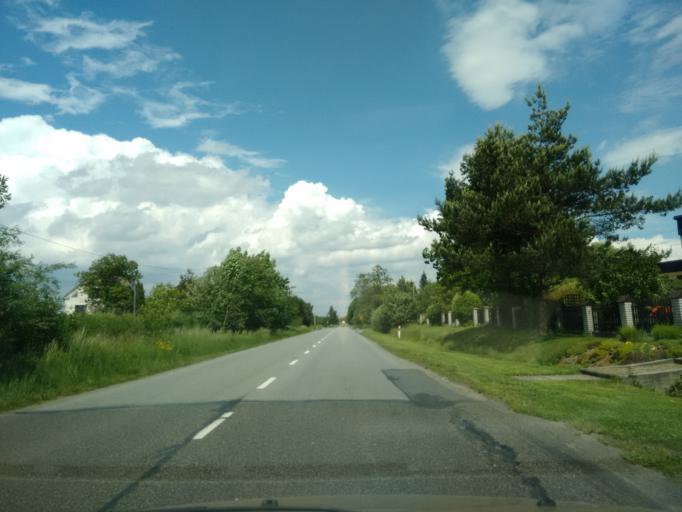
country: PL
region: Silesian Voivodeship
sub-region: Powiat cieszynski
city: Pruchna
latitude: 49.8487
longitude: 18.6723
